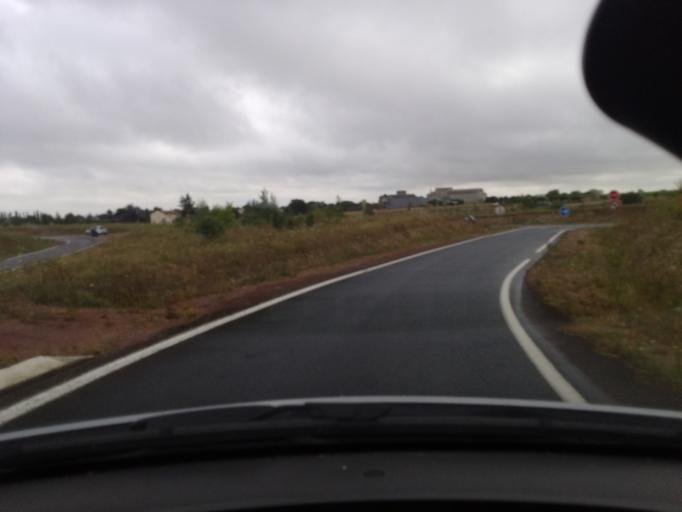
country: FR
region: Pays de la Loire
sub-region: Departement de la Vendee
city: Lucon
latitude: 46.4691
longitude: -1.1538
